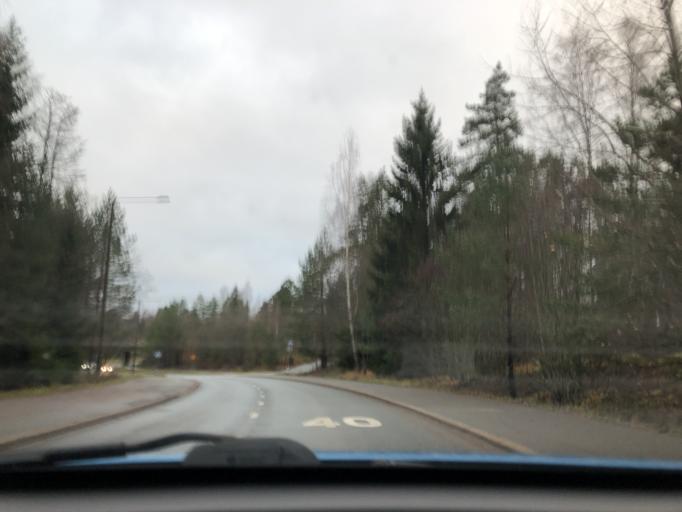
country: FI
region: Pirkanmaa
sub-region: Tampere
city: Kangasala
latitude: 61.5278
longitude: 24.0159
